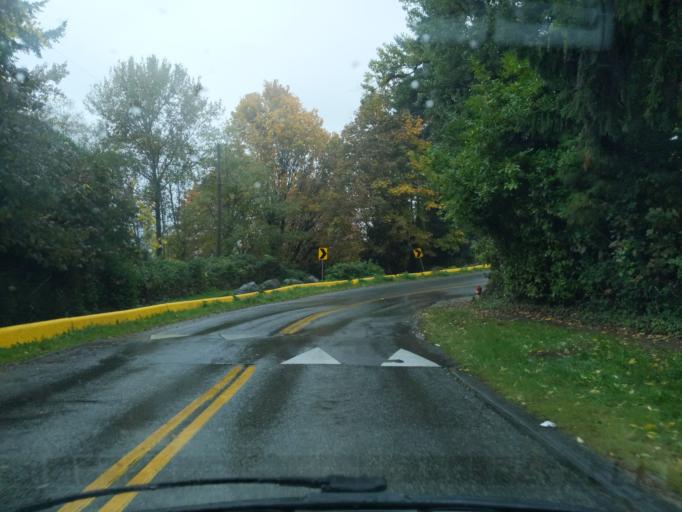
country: CA
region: British Columbia
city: New Westminster
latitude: 49.2003
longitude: -122.8672
